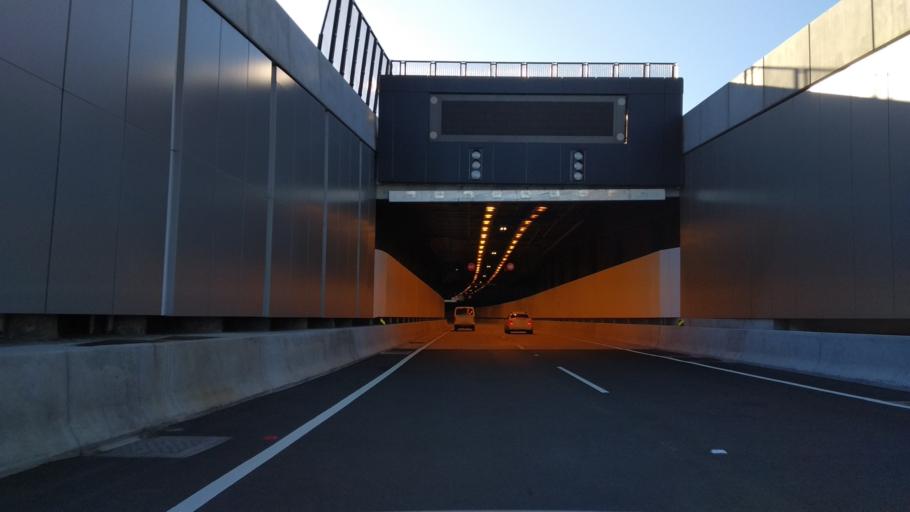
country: AU
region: New South Wales
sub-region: Ashfield
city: Summer Hill
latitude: -33.8823
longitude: 151.1328
